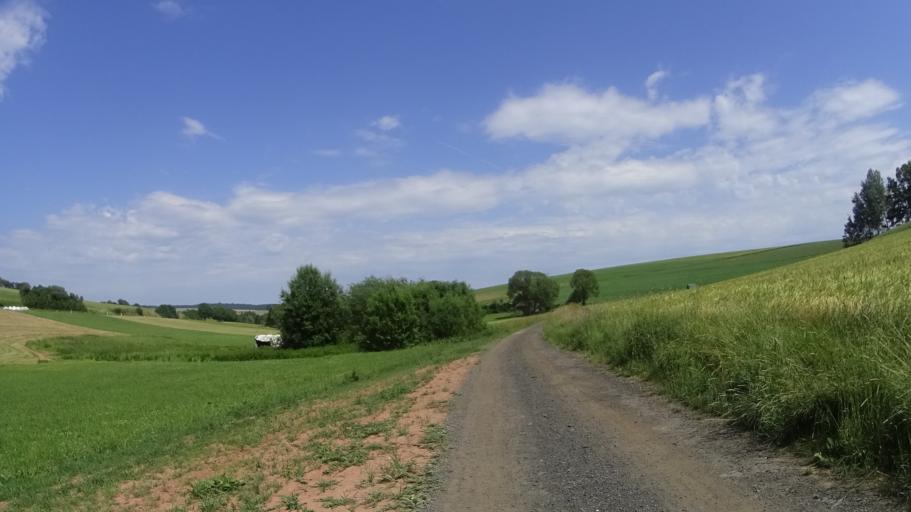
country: DE
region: Hesse
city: Rosenthal
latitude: 50.9700
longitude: 8.8461
